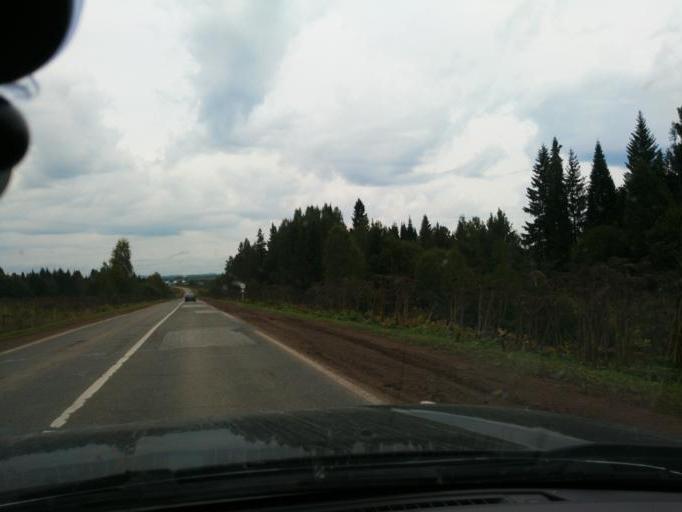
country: RU
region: Perm
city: Chernushka
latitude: 56.7190
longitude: 56.1803
